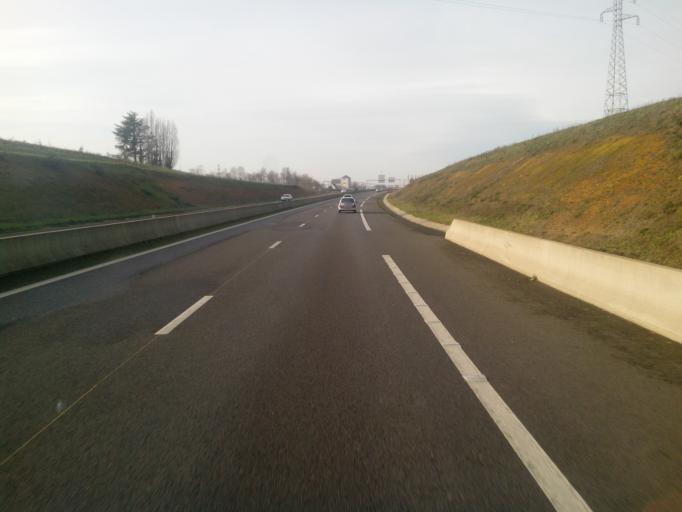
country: FR
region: Brittany
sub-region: Departement d'Ille-et-Vilaine
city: Vezin-le-Coquet
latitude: 48.1262
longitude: -1.7403
